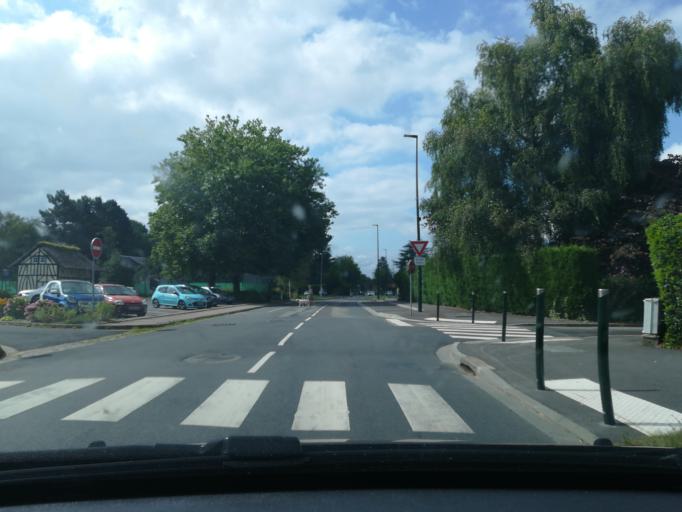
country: FR
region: Haute-Normandie
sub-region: Departement de la Seine-Maritime
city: Bois-Guillaume
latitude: 49.4689
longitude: 1.1168
